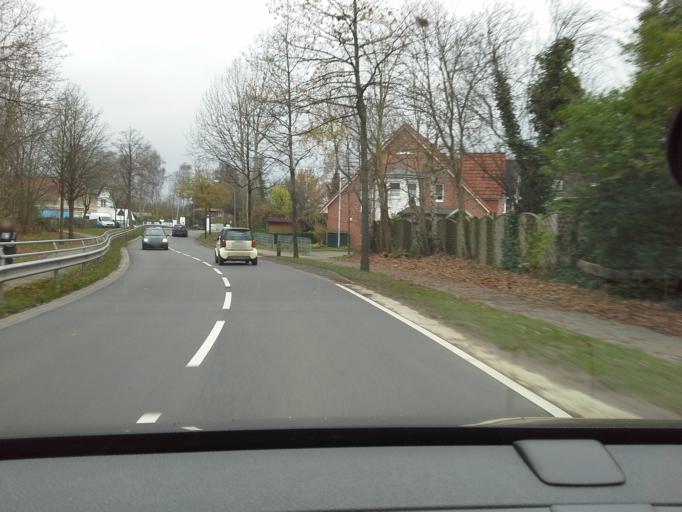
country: DE
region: Schleswig-Holstein
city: Kummerfeld
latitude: 53.6836
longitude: 9.7936
